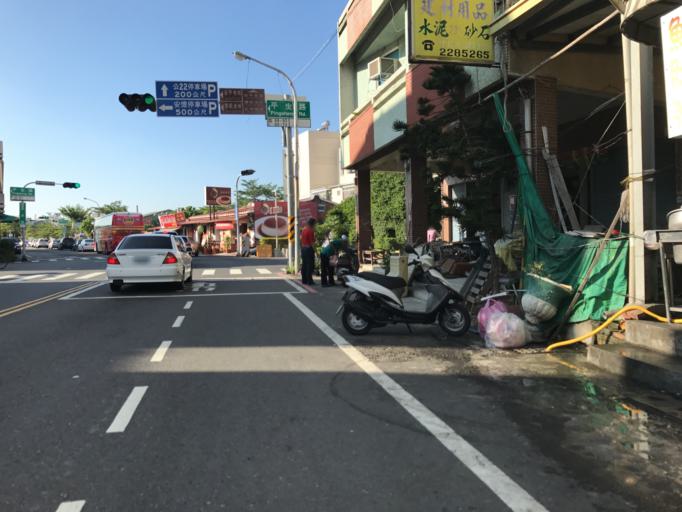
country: TW
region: Taiwan
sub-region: Tainan
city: Tainan
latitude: 23.0020
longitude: 120.1651
